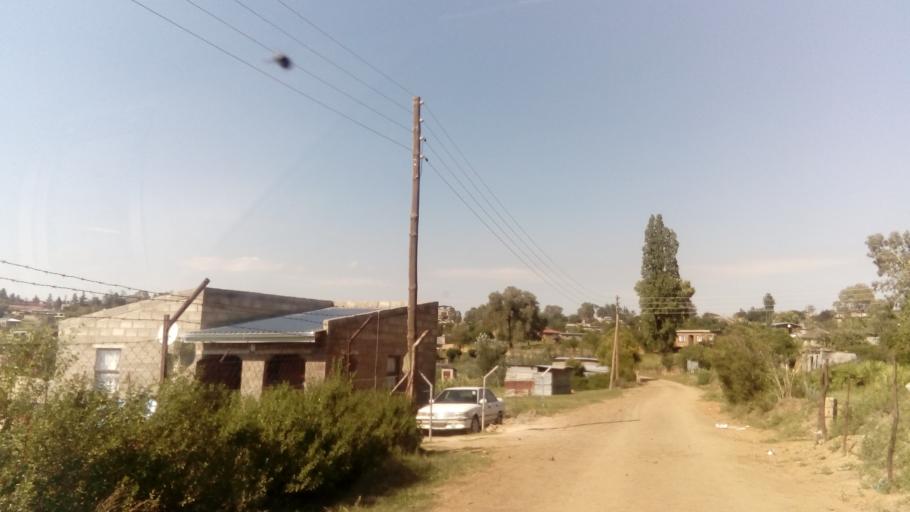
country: LS
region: Berea
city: Teyateyaneng
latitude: -29.1423
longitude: 27.7554
